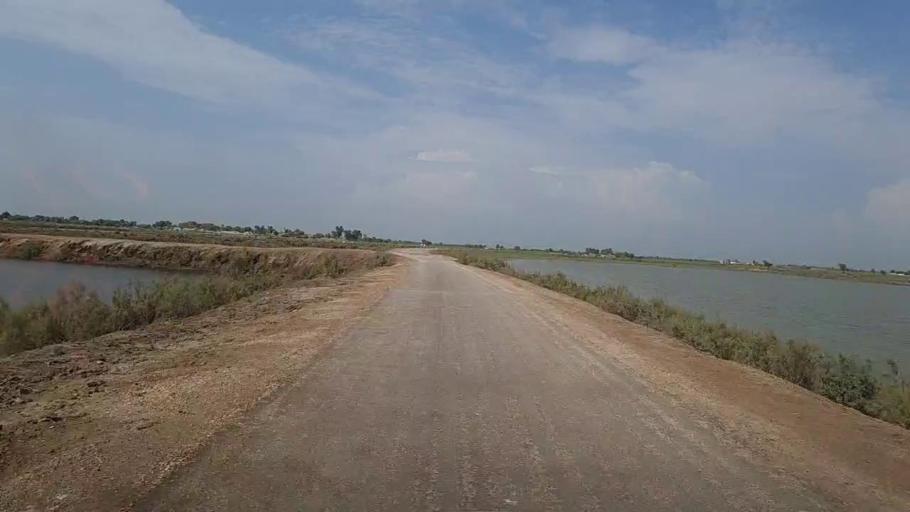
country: PK
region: Sindh
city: Thul
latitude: 28.2852
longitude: 68.8233
